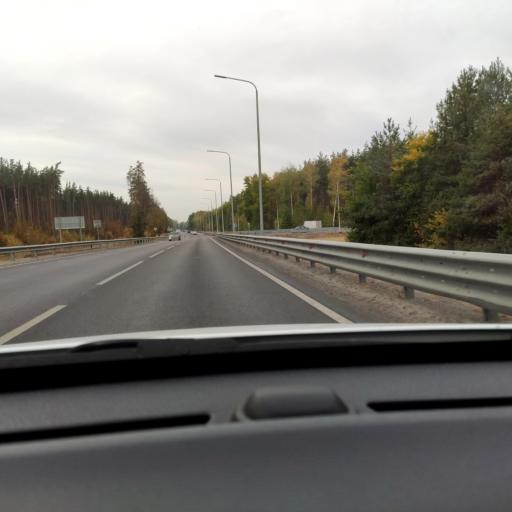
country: RU
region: Voronezj
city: Somovo
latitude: 51.6915
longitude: 39.3018
